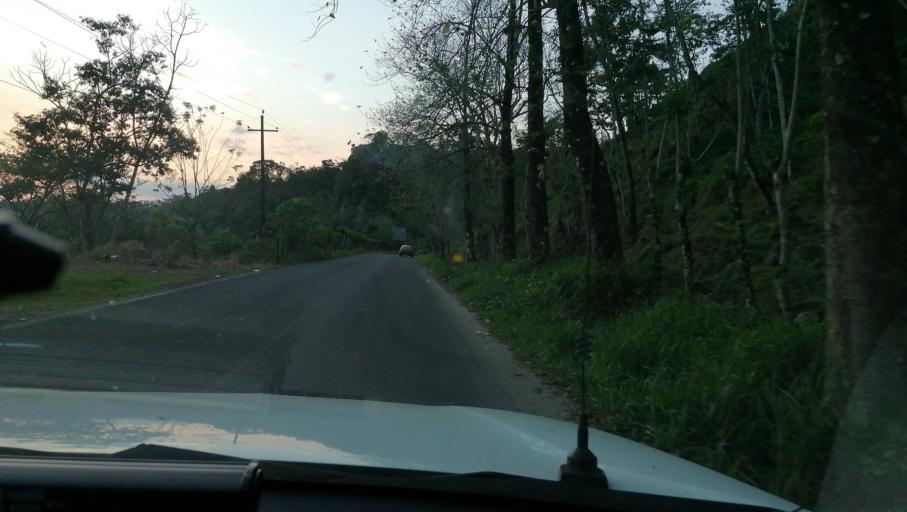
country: MX
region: Chiapas
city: Ostuacan
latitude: 17.4165
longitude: -93.3404
